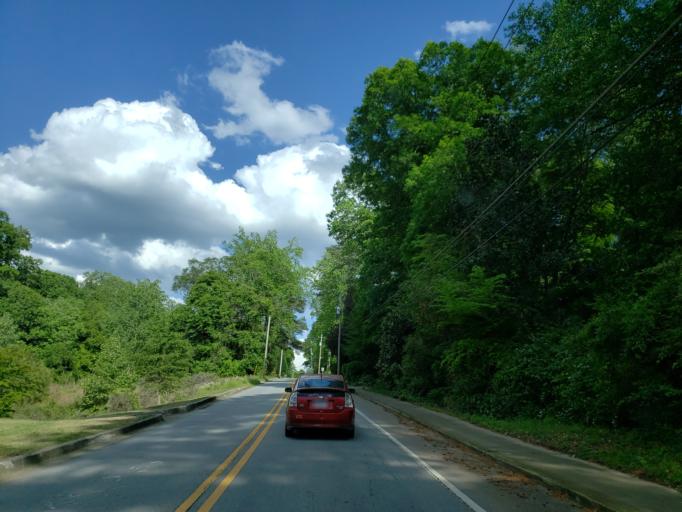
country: US
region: Georgia
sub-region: DeKalb County
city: North Druid Hills
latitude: 33.8470
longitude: -84.2782
